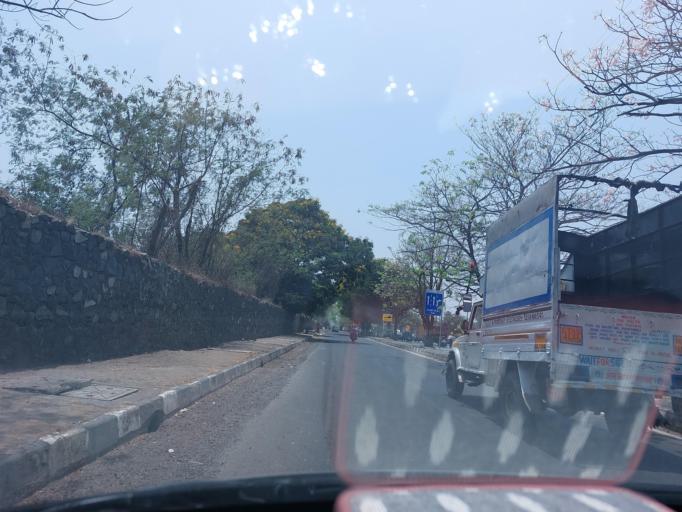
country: IN
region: Maharashtra
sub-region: Mumbai Suburban
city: Powai
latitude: 19.1025
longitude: 72.9300
